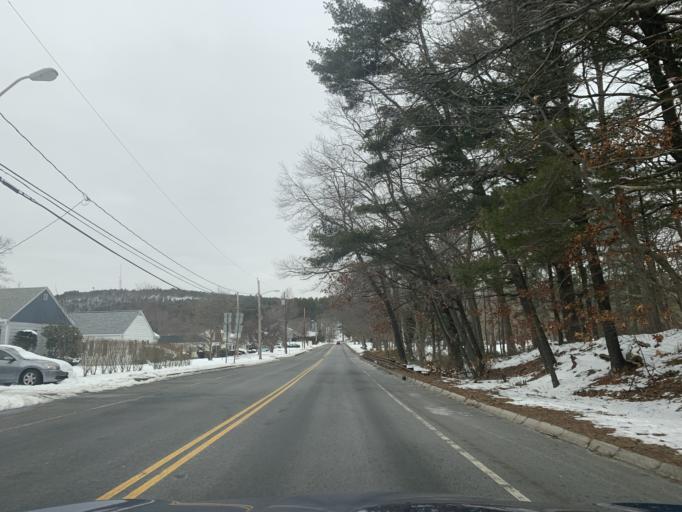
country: US
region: Massachusetts
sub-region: Norfolk County
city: Milton
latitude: 42.2058
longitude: -71.0992
